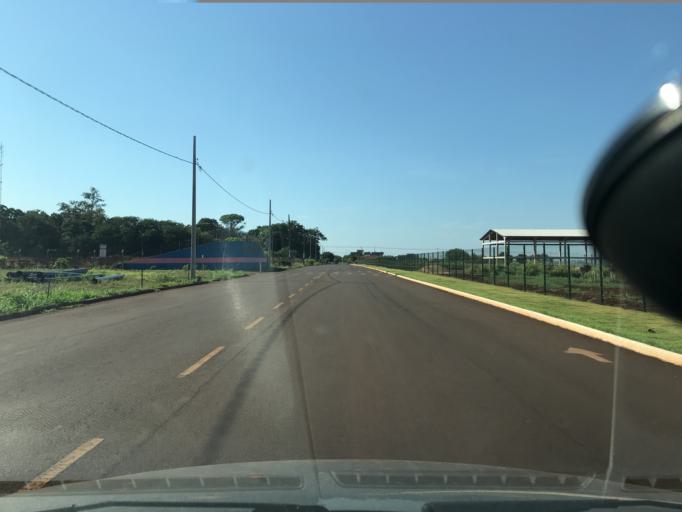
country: BR
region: Parana
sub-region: Palotina
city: Palotina
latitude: -24.2944
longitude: -53.8401
